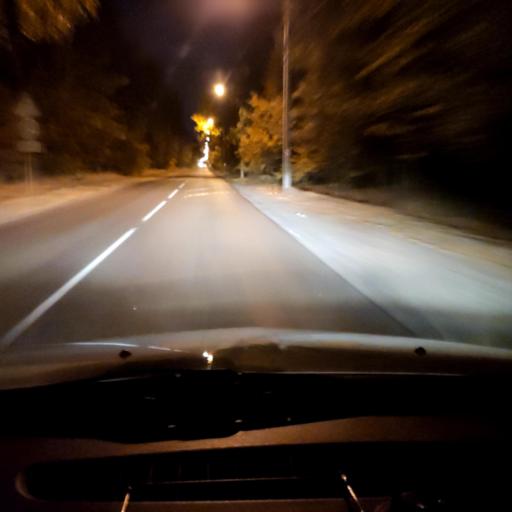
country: RU
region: Voronezj
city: Somovo
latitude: 51.7085
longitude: 39.3258
